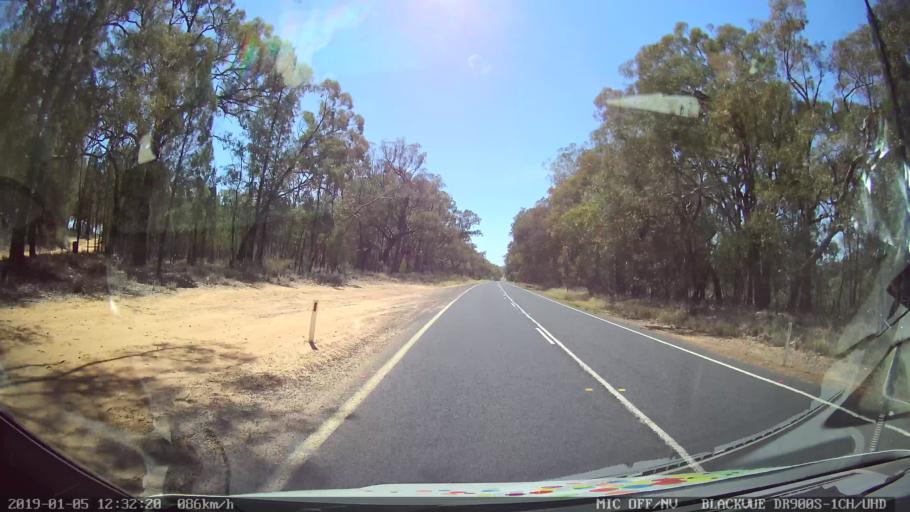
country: AU
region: New South Wales
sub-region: Warrumbungle Shire
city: Coonabarabran
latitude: -31.2175
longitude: 149.3782
